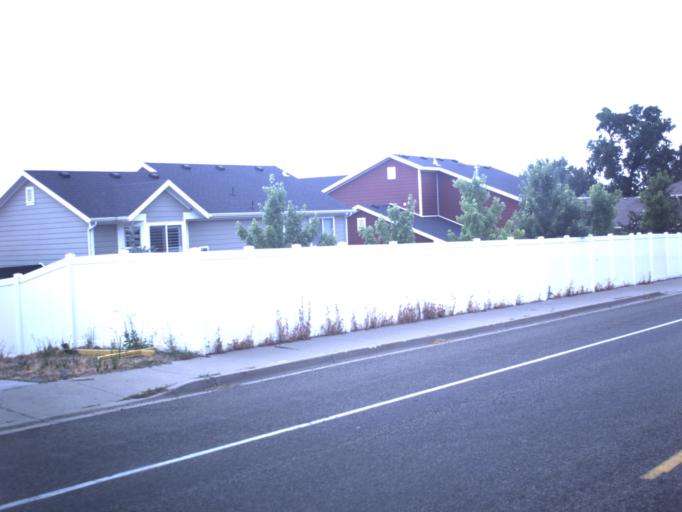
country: US
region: Utah
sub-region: Davis County
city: Farmington
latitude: 40.9534
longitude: -111.8833
